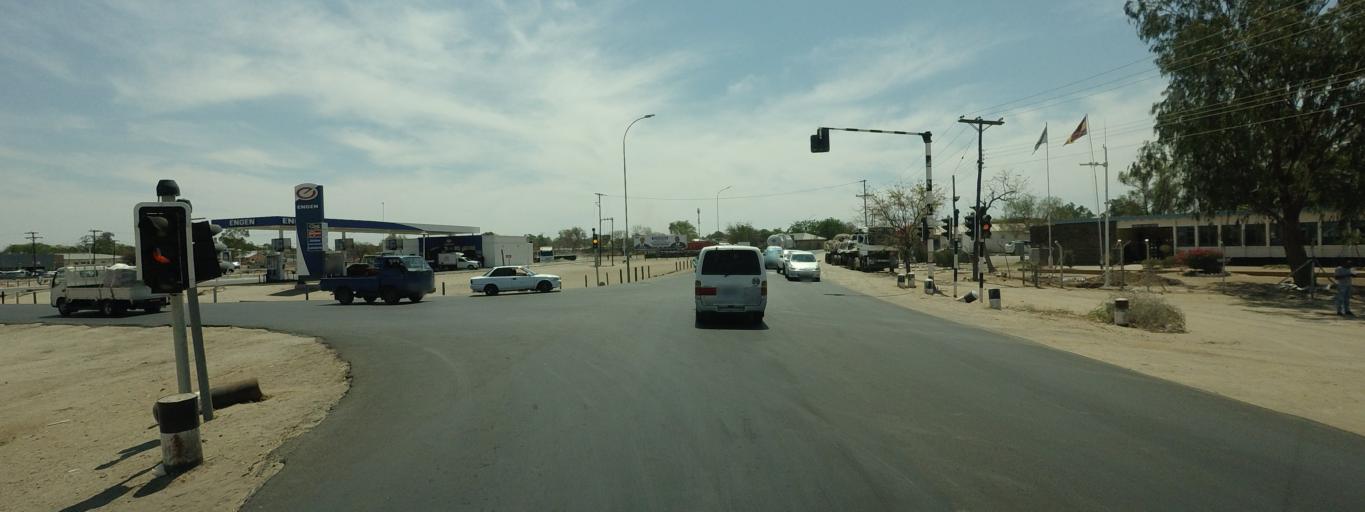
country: BW
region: North East
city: Francistown
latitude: -21.1699
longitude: 27.4969
